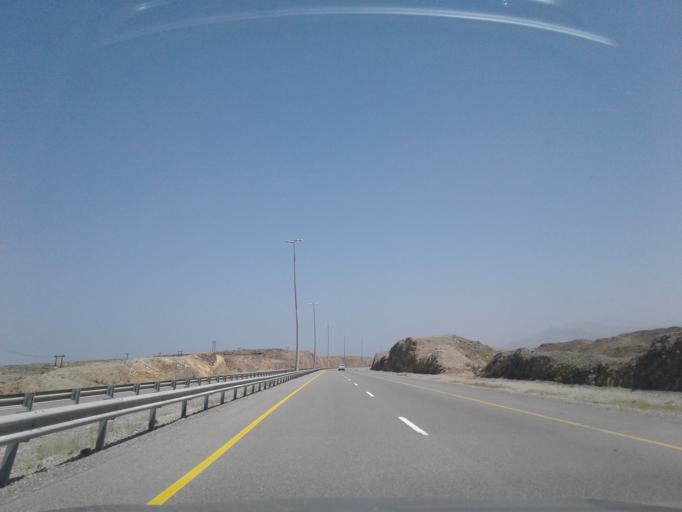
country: OM
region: Muhafazat Masqat
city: Muscat
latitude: 23.2018
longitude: 58.8245
